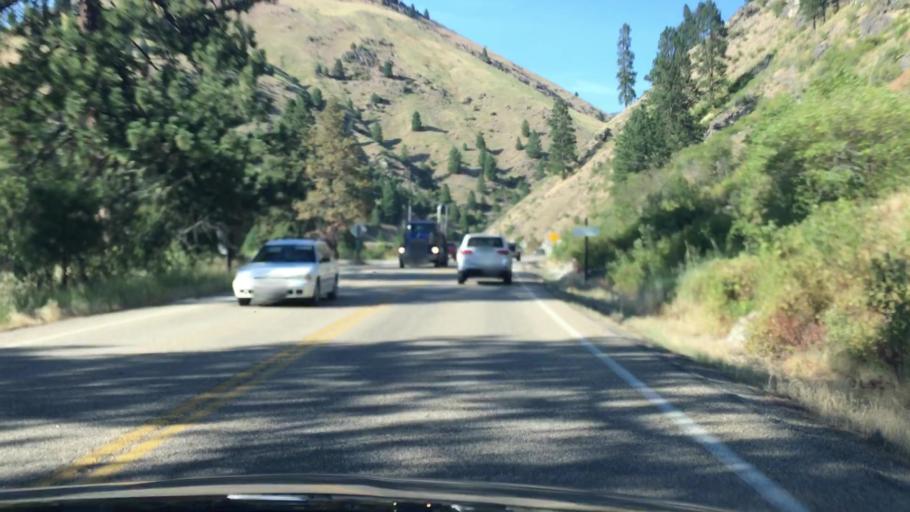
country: US
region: Idaho
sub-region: Boise County
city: Idaho City
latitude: 44.0865
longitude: -116.1134
